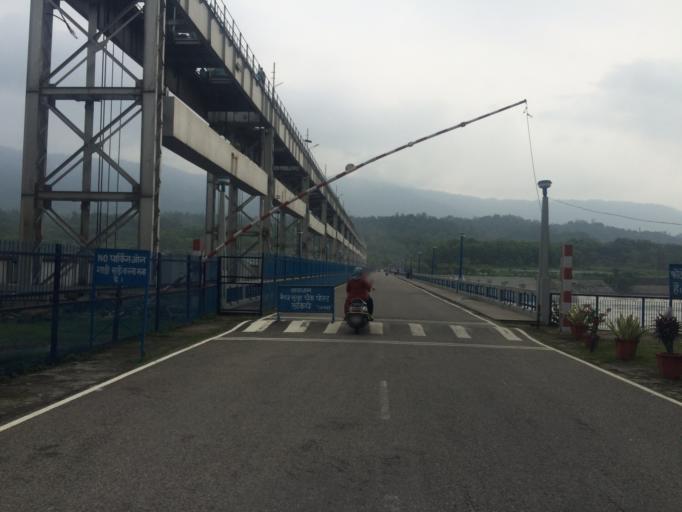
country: IN
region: Uttarakhand
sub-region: Dehradun
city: Birbhaddar
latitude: 30.0747
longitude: 78.2871
